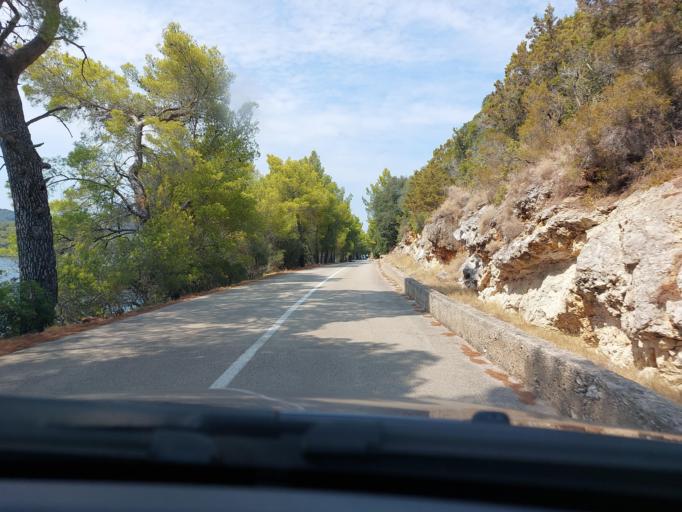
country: HR
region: Dubrovacko-Neretvanska
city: Smokvica
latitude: 42.7566
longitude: 16.8234
